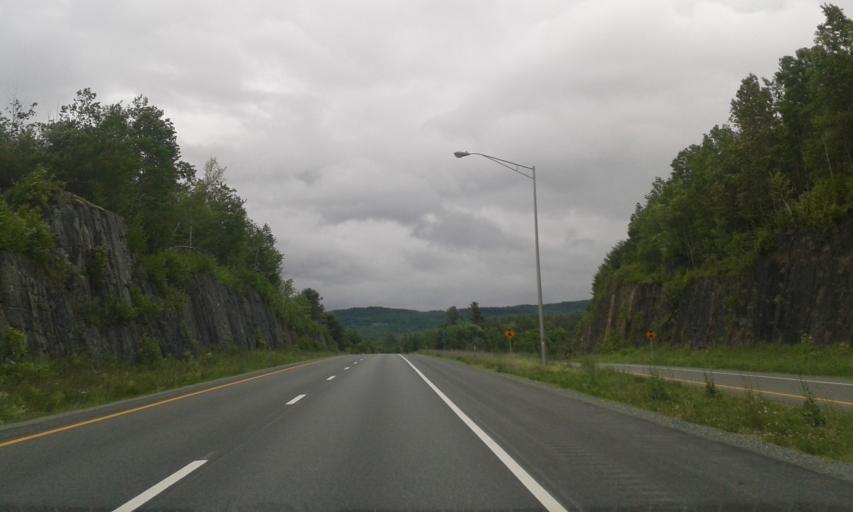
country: US
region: New Hampshire
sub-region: Grafton County
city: Littleton
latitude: 44.3314
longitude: -71.8797
